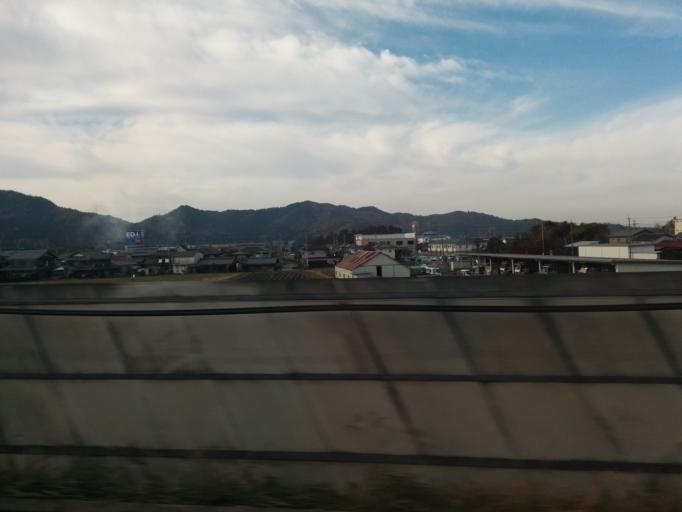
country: JP
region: Shiga Prefecture
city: Youkaichi
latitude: 35.1473
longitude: 136.1902
